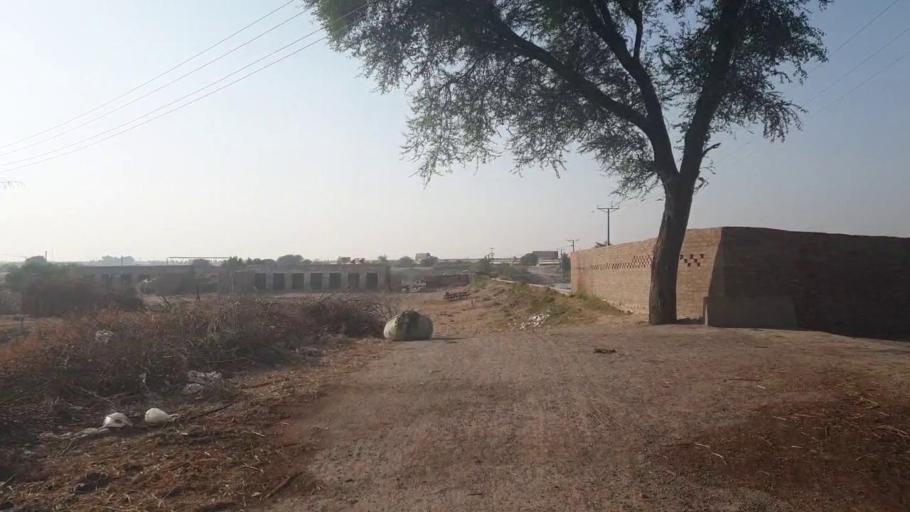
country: PK
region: Sindh
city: Jamshoro
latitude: 25.4014
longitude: 68.2904
